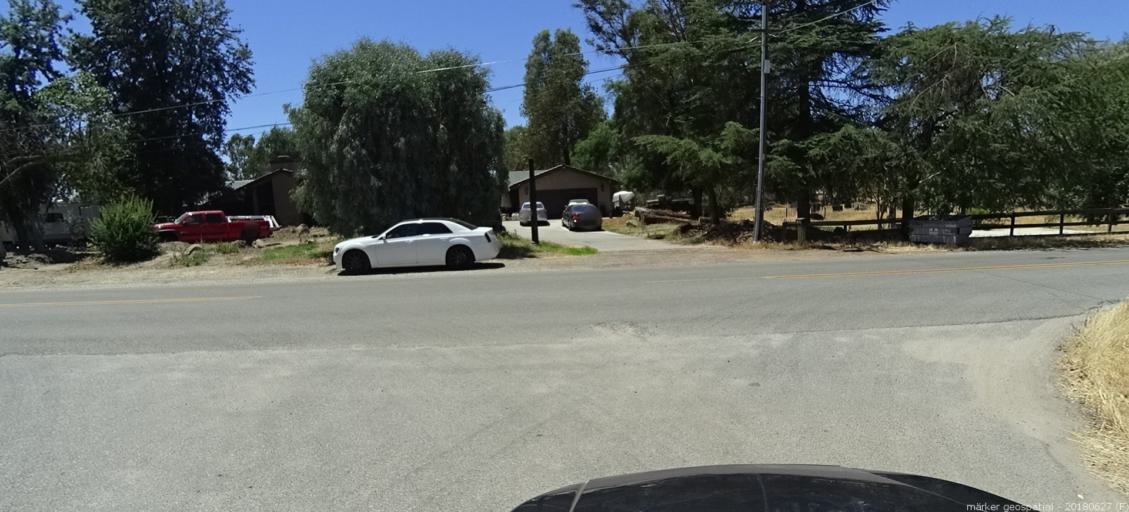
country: US
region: California
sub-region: Madera County
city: Bonadelle Ranchos-Madera Ranchos
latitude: 36.9279
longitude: -119.8624
